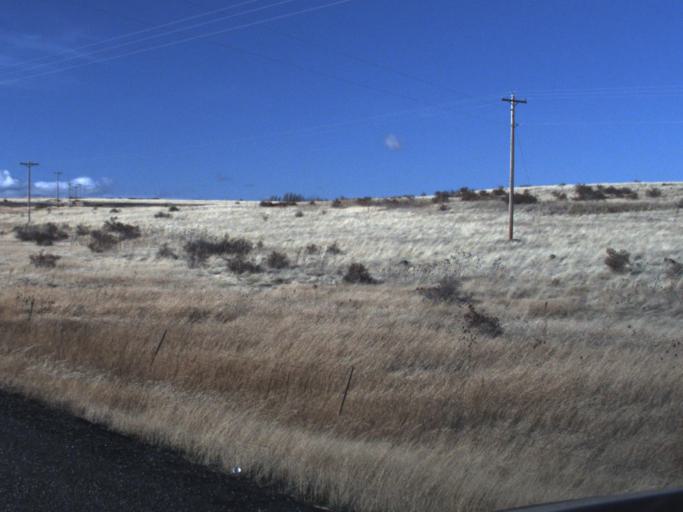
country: US
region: Washington
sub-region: Asotin County
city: Asotin
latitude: 46.1626
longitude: -117.0992
